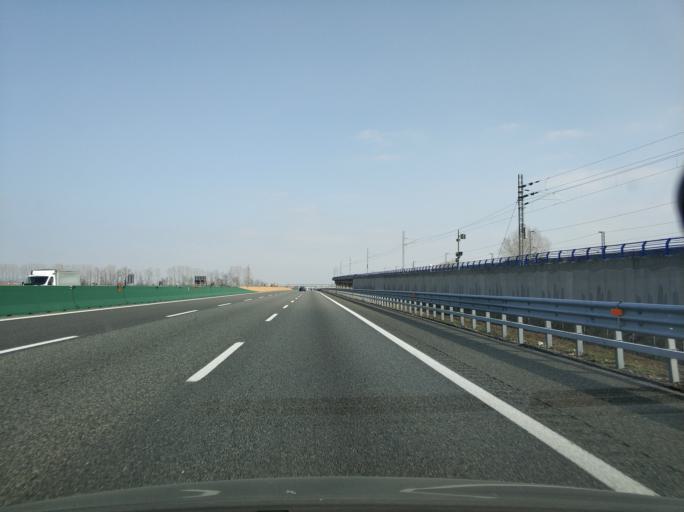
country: IT
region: Piedmont
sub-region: Provincia di Vercelli
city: Cigliano
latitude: 45.2979
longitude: 8.0474
